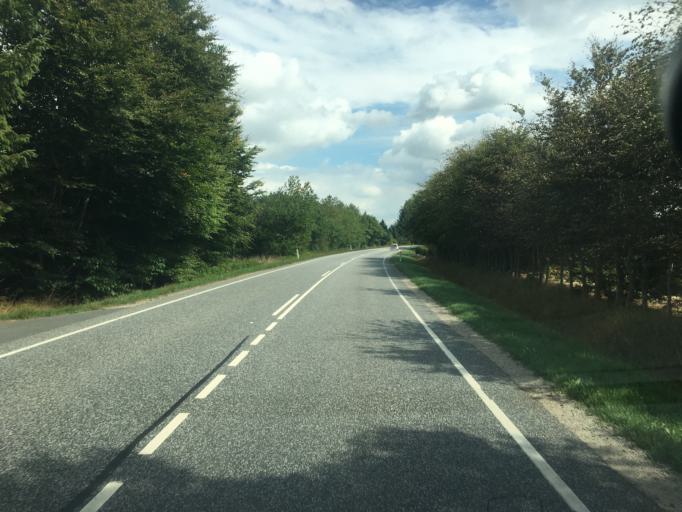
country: DK
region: South Denmark
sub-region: Aabenraa Kommune
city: Rodekro
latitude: 54.9821
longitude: 9.3476
